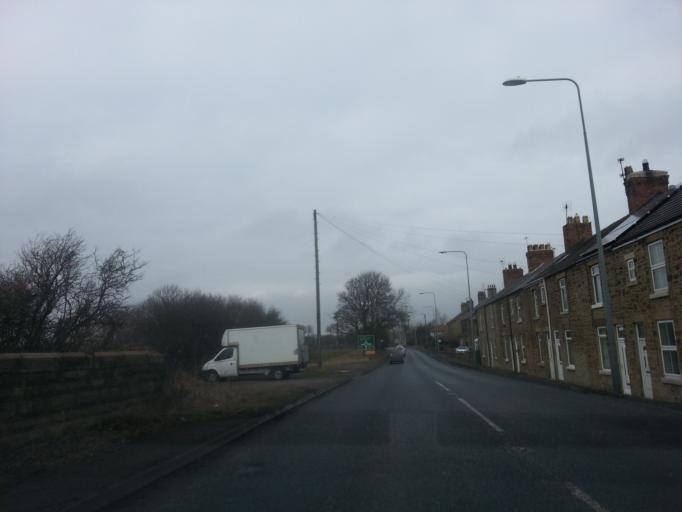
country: GB
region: England
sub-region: County Durham
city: High Etherley
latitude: 54.6237
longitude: -1.7100
